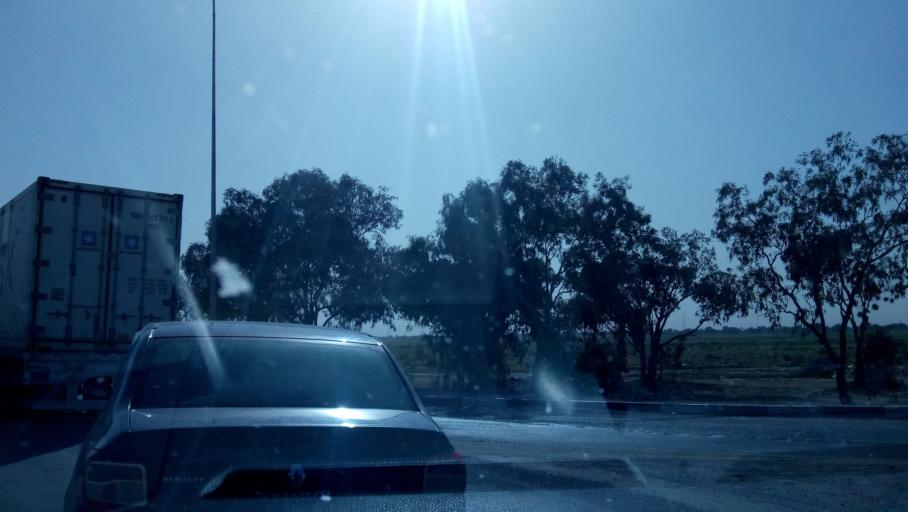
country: TN
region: Qabis
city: Gabes
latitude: 33.8880
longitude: 10.0216
